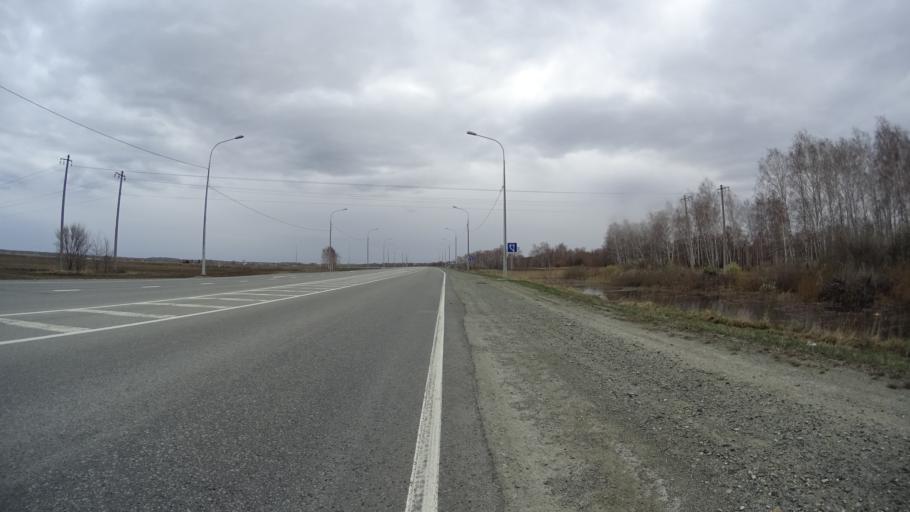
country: RU
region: Chelyabinsk
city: Krasnogorskiy
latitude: 54.6851
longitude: 61.2475
